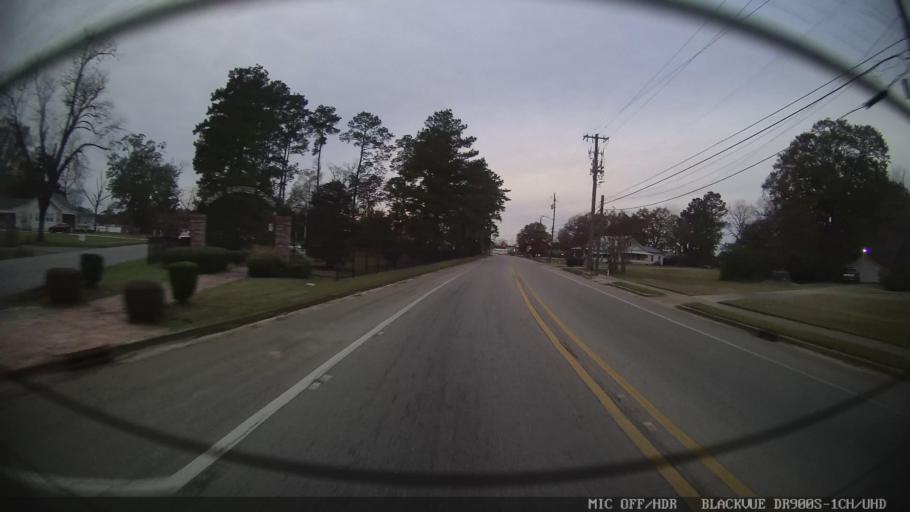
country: US
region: Mississippi
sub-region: Clarke County
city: Quitman
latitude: 32.0366
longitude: -88.7254
